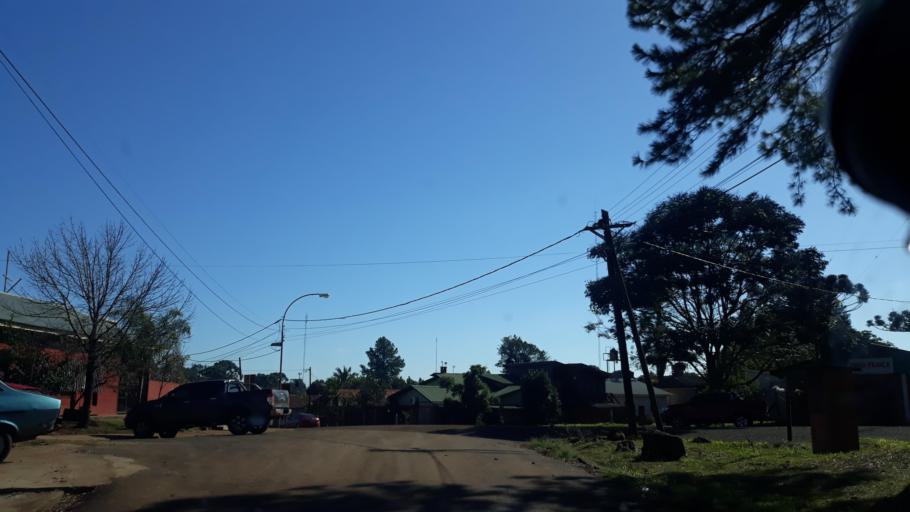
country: AR
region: Misiones
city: Bernardo de Irigoyen
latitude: -26.2589
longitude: -53.6459
